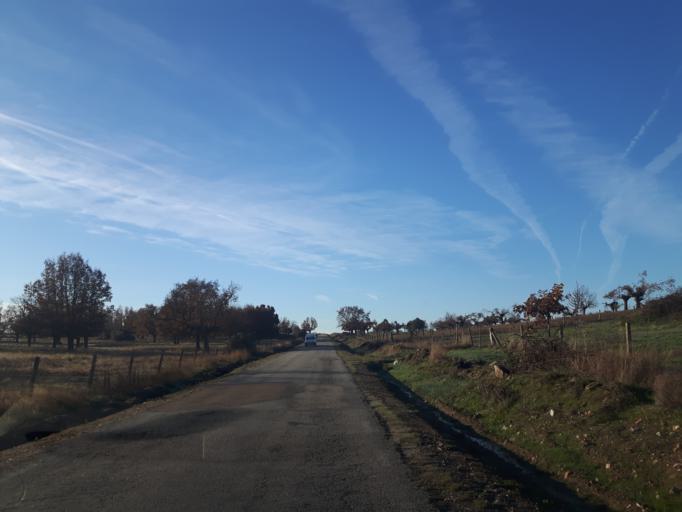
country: ES
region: Castille and Leon
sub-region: Provincia de Salamanca
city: Cerralbo
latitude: 40.9670
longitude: -6.5914
